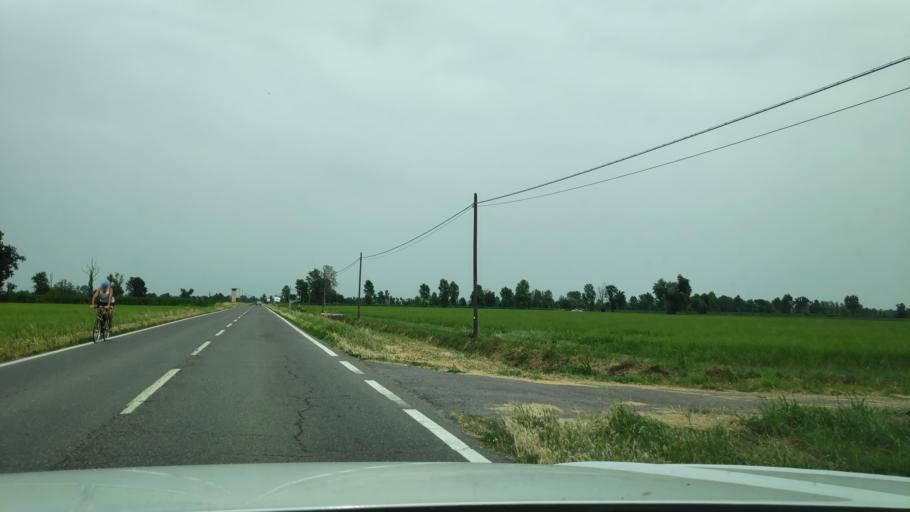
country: IT
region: Lombardy
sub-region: Provincia di Cremona
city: Ricengo
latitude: 45.4159
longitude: 9.7470
